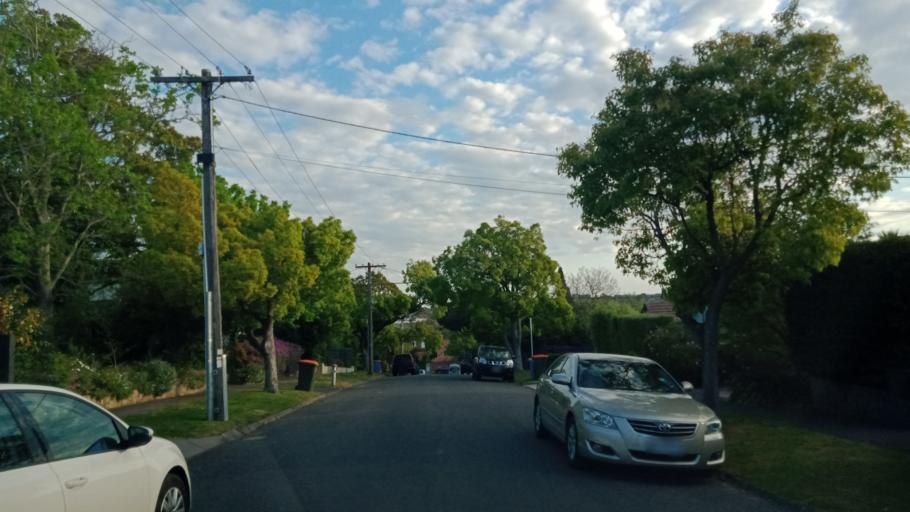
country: AU
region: Victoria
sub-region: Boroondara
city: Camberwell
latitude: -37.8450
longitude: 145.0587
